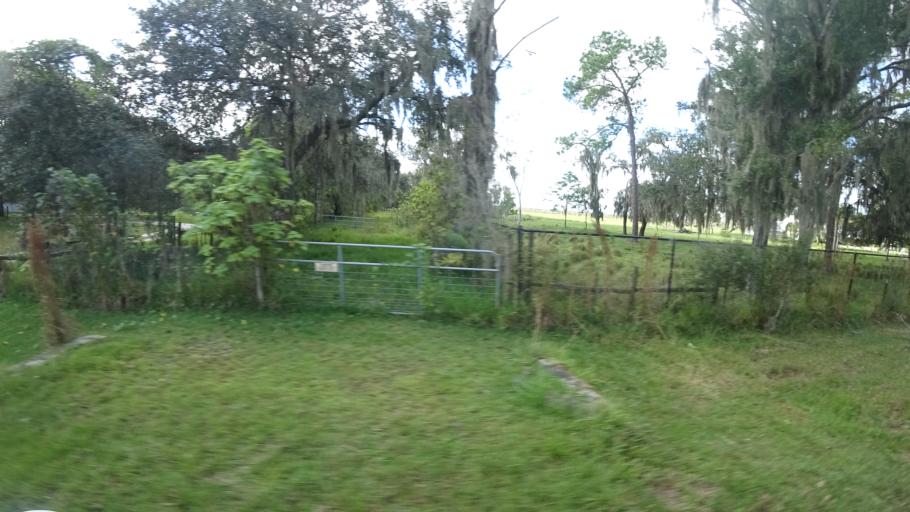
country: US
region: Florida
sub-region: Sarasota County
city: Lake Sarasota
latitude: 27.3442
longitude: -82.2248
